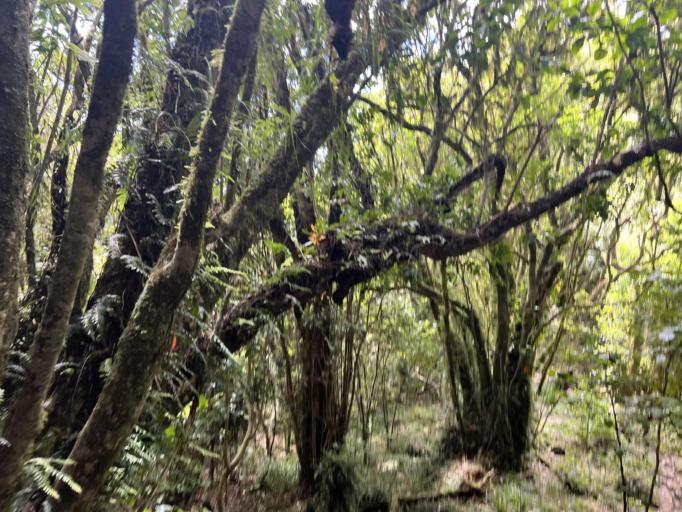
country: NZ
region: Wellington
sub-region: Kapiti Coast District
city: Paraparaumu
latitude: -40.8794
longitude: 175.0911
